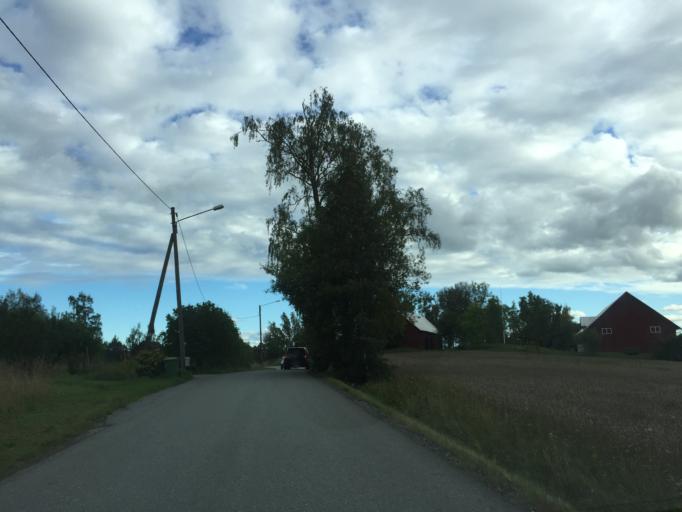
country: SE
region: OErebro
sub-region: Orebro Kommun
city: Hovsta
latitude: 59.3216
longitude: 15.2054
